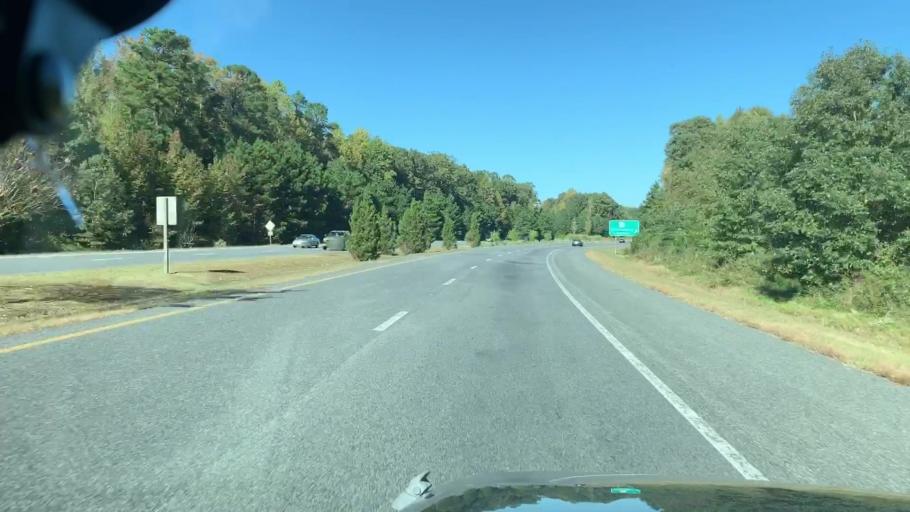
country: US
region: Virginia
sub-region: James City County
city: Williamsburg
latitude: 37.3312
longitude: -76.7550
